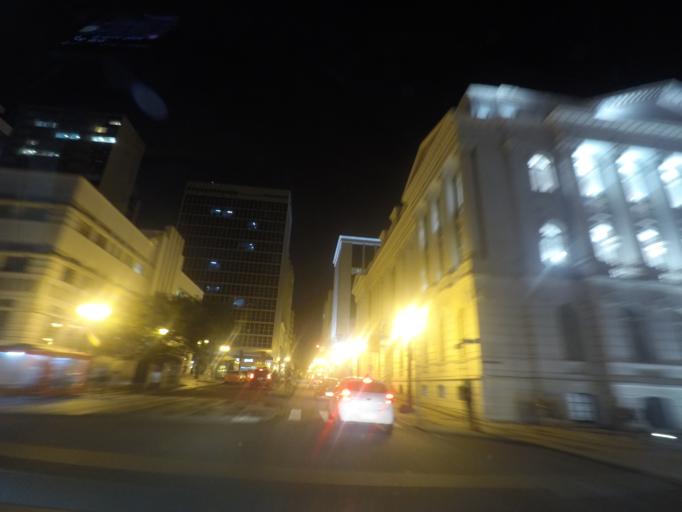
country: BR
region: Parana
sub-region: Curitiba
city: Curitiba
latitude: -25.4294
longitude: -49.2671
